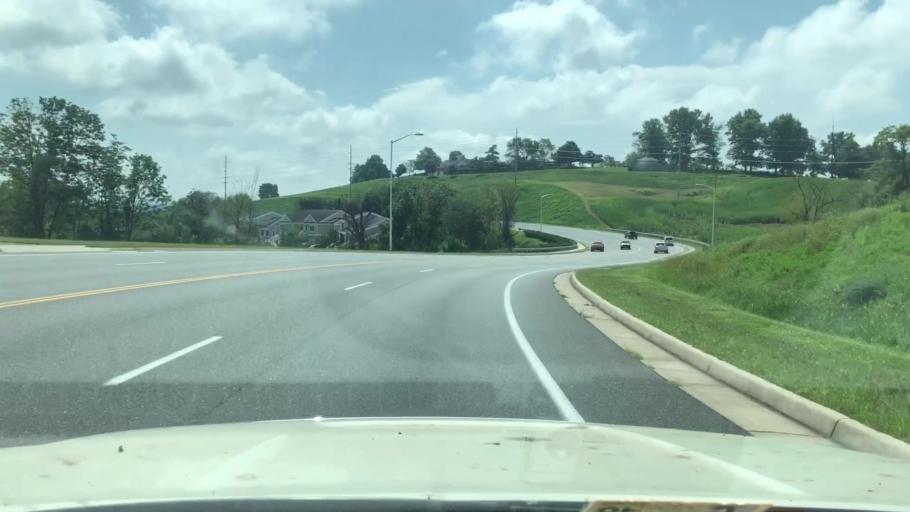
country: US
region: Virginia
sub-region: City of Harrisonburg
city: Harrisonburg
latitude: 38.4283
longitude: -78.9003
